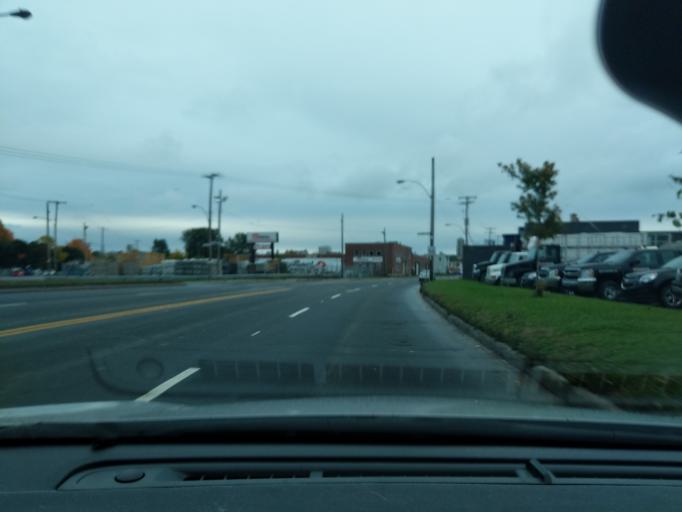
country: CA
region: Quebec
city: Quebec
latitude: 46.8064
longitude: -71.2672
